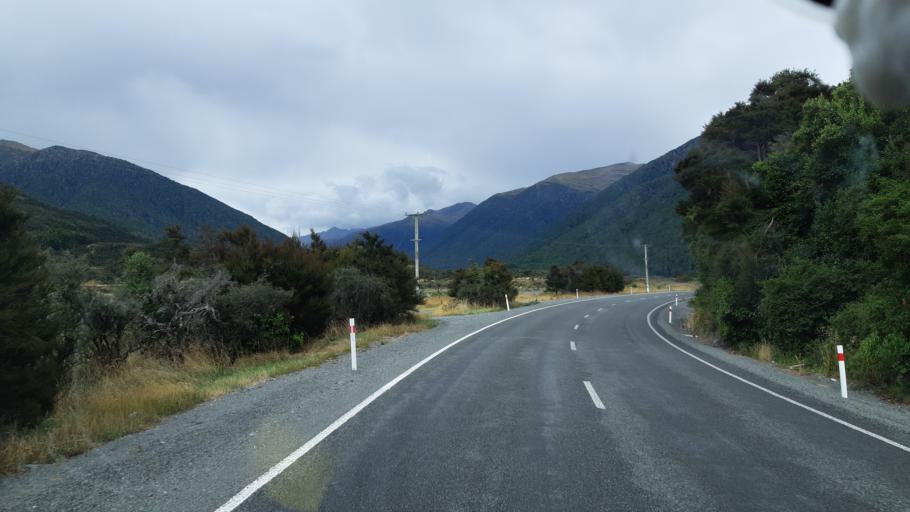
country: NZ
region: Canterbury
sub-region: Hurunui District
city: Amberley
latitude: -42.5562
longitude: 172.3492
